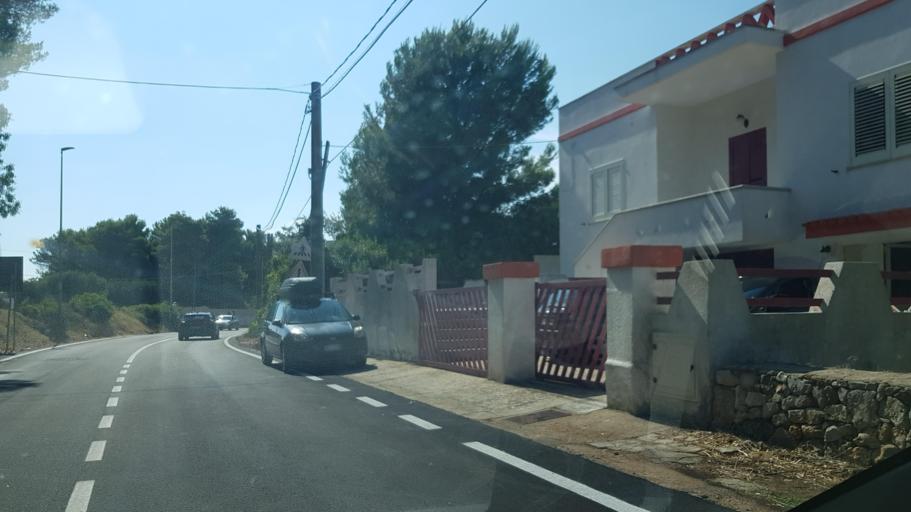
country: IT
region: Apulia
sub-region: Provincia di Lecce
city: Patu
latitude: 39.8093
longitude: 18.3246
